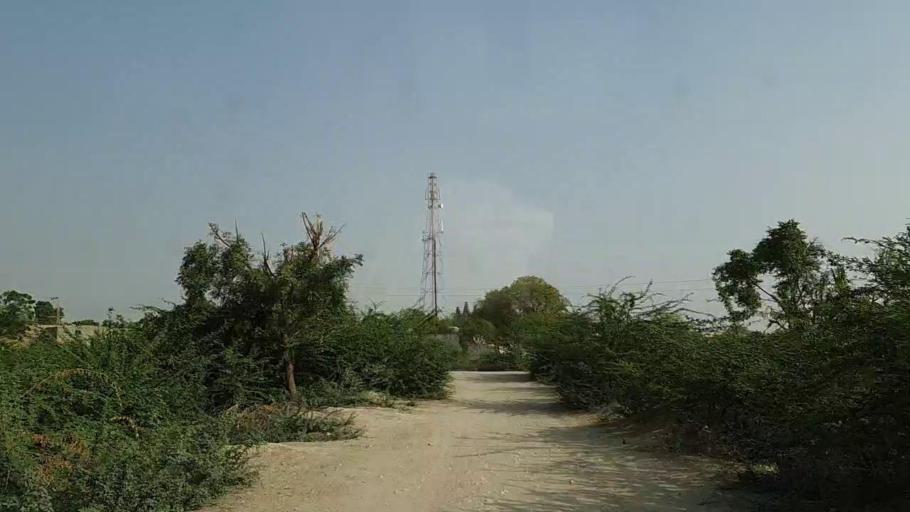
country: PK
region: Sindh
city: Naukot
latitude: 24.6591
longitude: 69.2884
